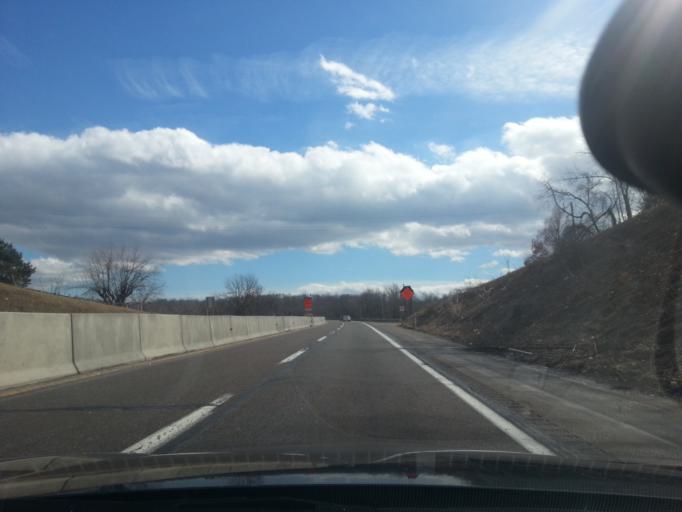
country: US
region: Pennsylvania
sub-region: Lehigh County
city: Emmaus
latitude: 40.5072
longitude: -75.5021
